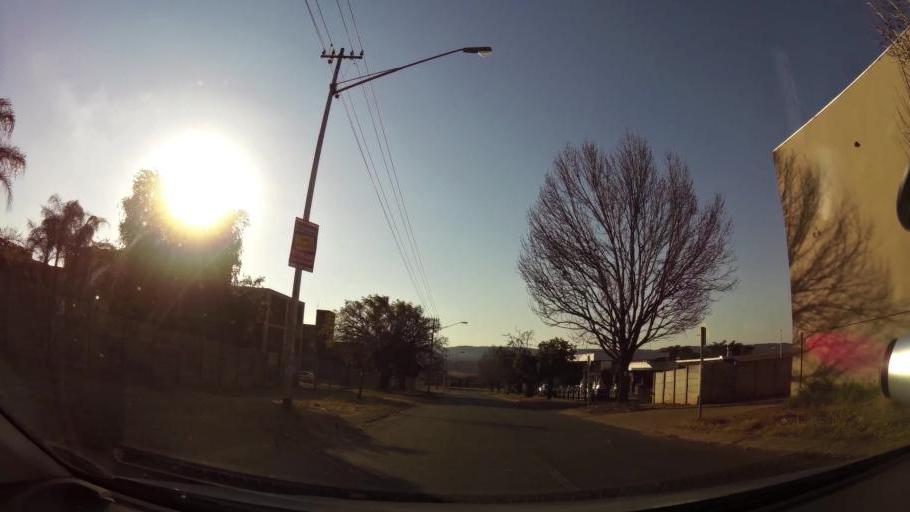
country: ZA
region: Gauteng
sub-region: City of Tshwane Metropolitan Municipality
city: Pretoria
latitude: -25.7569
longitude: 28.1146
